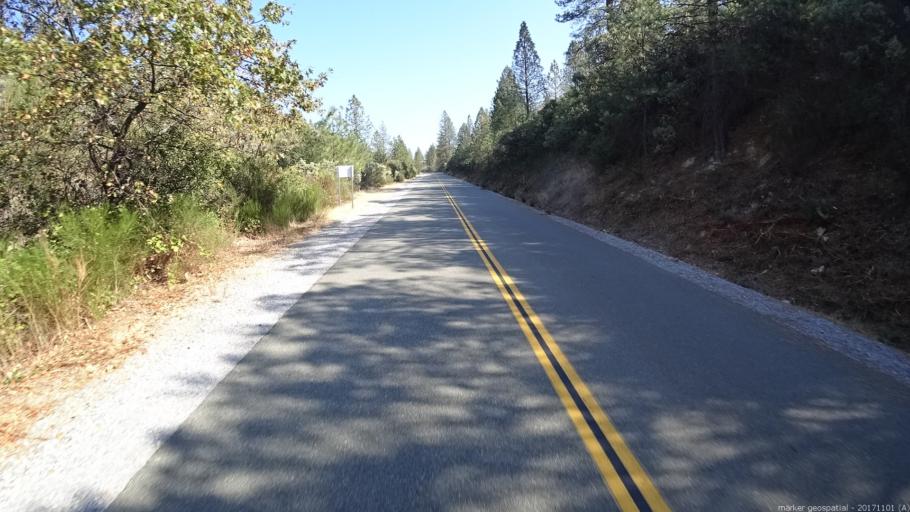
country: US
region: California
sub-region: Shasta County
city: Central Valley (historical)
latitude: 40.7143
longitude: -122.4356
